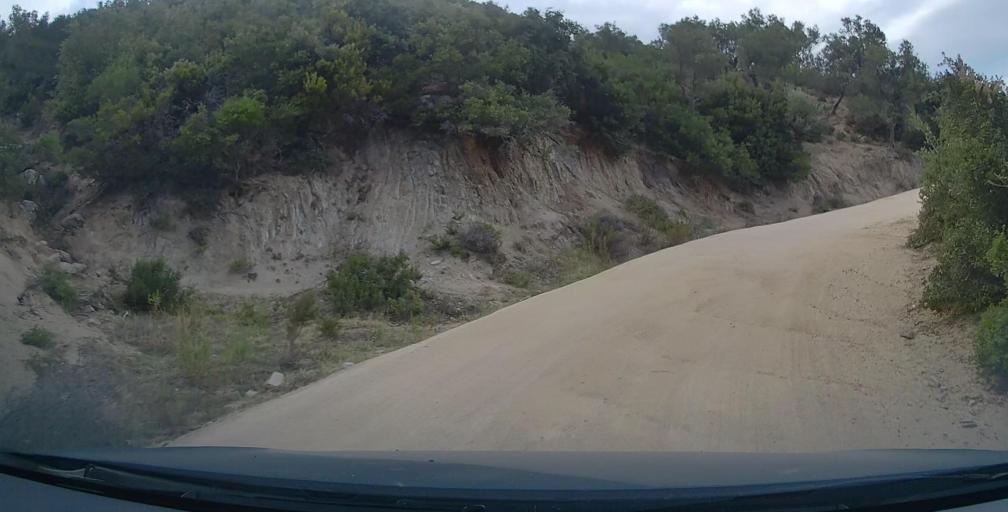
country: GR
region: Central Macedonia
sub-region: Nomos Chalkidikis
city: Sykia
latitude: 40.0140
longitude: 23.9369
